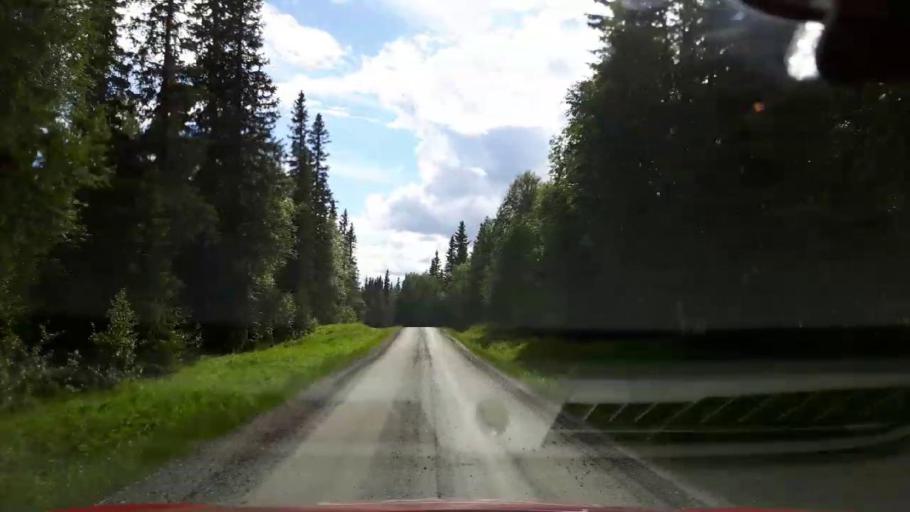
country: SE
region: Jaemtland
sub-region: Krokoms Kommun
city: Valla
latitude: 63.8548
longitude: 14.0916
